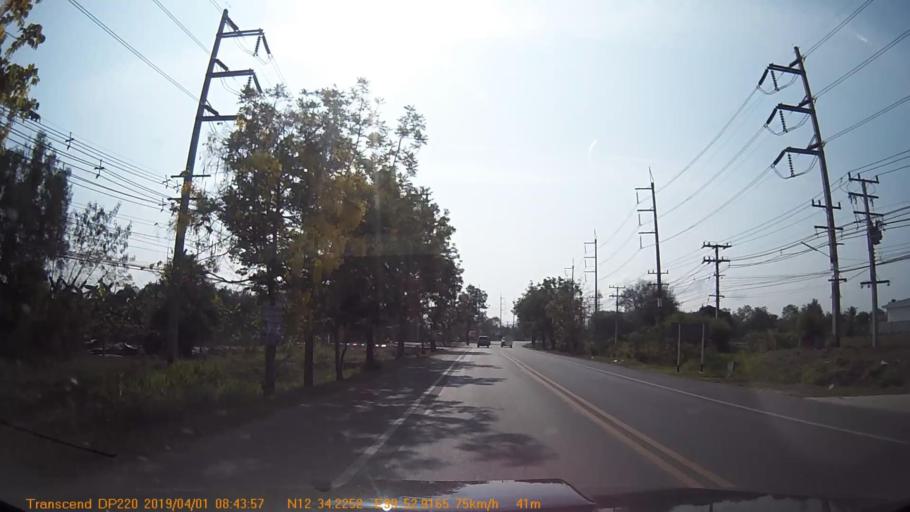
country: TH
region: Prachuap Khiri Khan
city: Hua Hin
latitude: 12.5703
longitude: 99.8823
